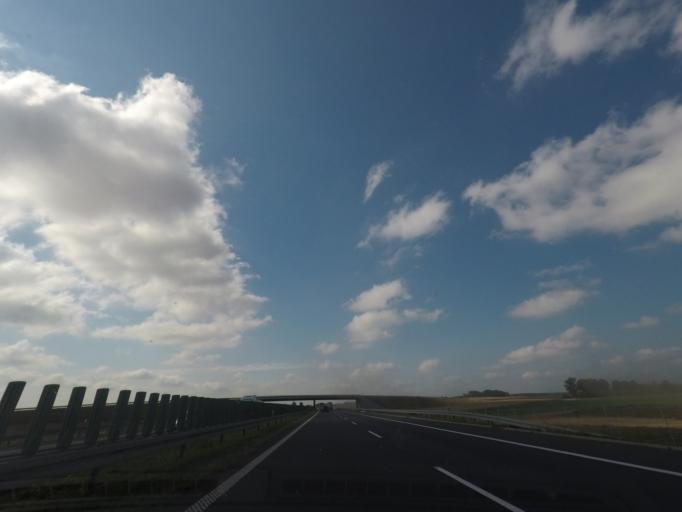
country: PL
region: Pomeranian Voivodeship
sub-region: Powiat starogardzki
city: Smetowo Graniczne
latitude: 53.7056
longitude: 18.6284
